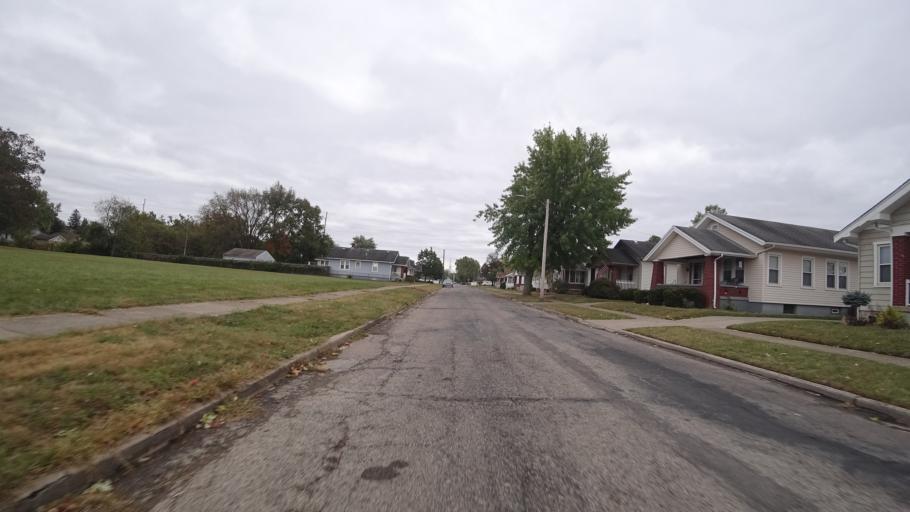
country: US
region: Ohio
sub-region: Butler County
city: Fairfield
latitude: 39.3686
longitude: -84.5605
